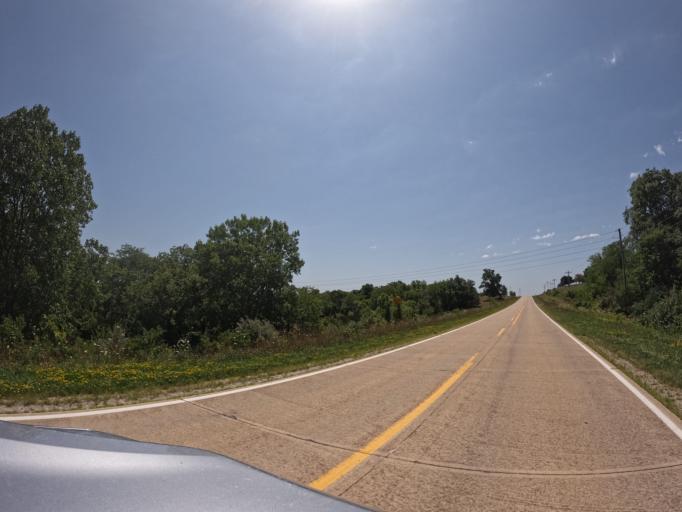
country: US
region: Iowa
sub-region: Henry County
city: Mount Pleasant
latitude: 40.9381
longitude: -91.5545
